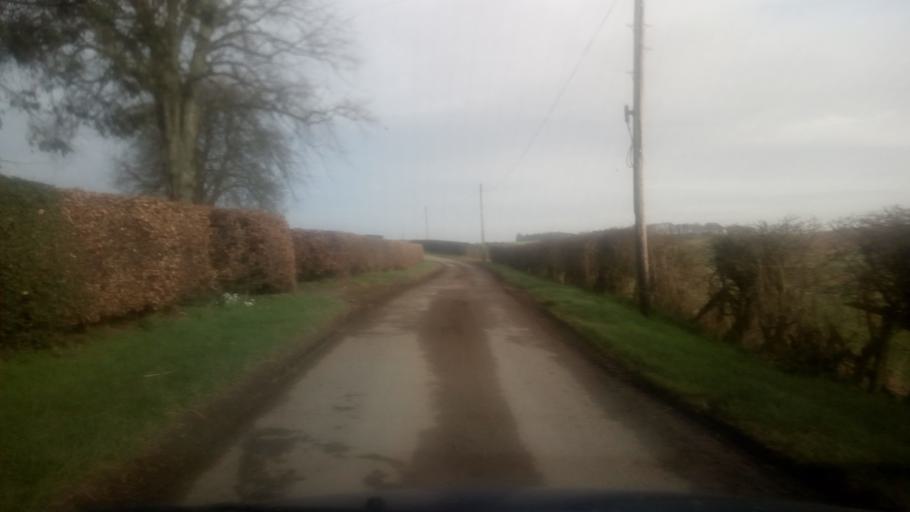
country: GB
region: Scotland
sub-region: The Scottish Borders
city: Hawick
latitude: 55.4338
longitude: -2.6966
